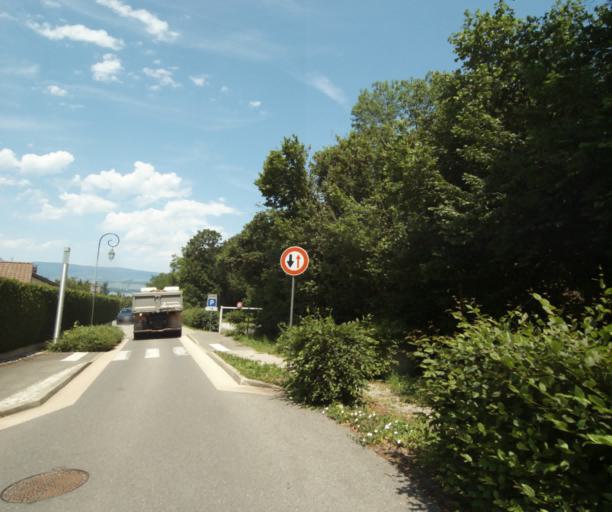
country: FR
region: Rhone-Alpes
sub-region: Departement de la Haute-Savoie
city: Messery
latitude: 46.3613
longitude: 6.3058
